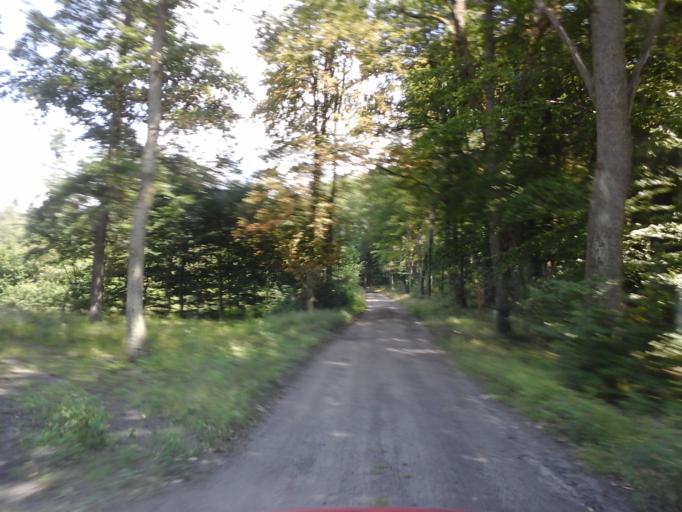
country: PL
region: West Pomeranian Voivodeship
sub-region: Powiat choszczenski
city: Bierzwnik
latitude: 53.0686
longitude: 15.6690
